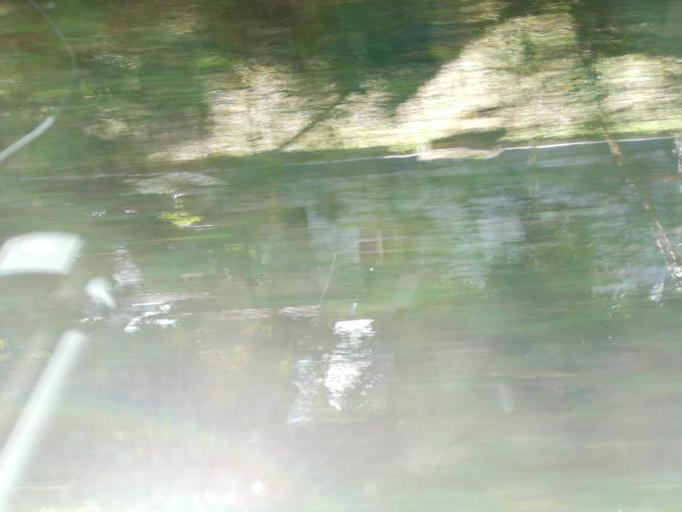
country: MU
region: Moka
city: Moka
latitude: -20.2260
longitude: 57.4737
